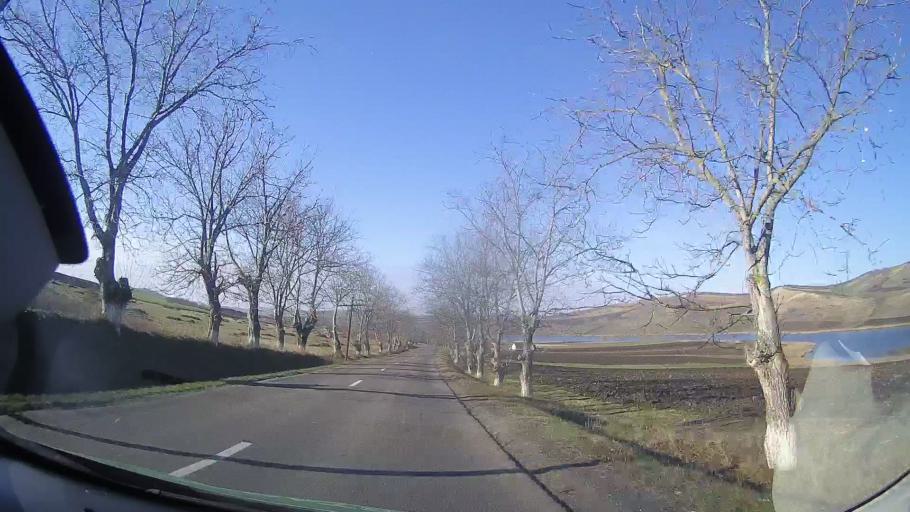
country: RO
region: Mures
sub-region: Comuna Saulia
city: Saulia
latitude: 46.6497
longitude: 24.2014
